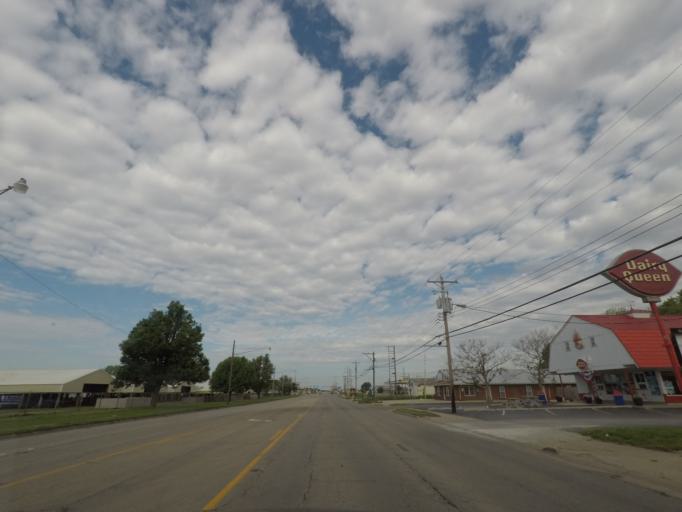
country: US
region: Illinois
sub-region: Logan County
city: Lincoln
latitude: 40.1578
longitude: -89.3828
